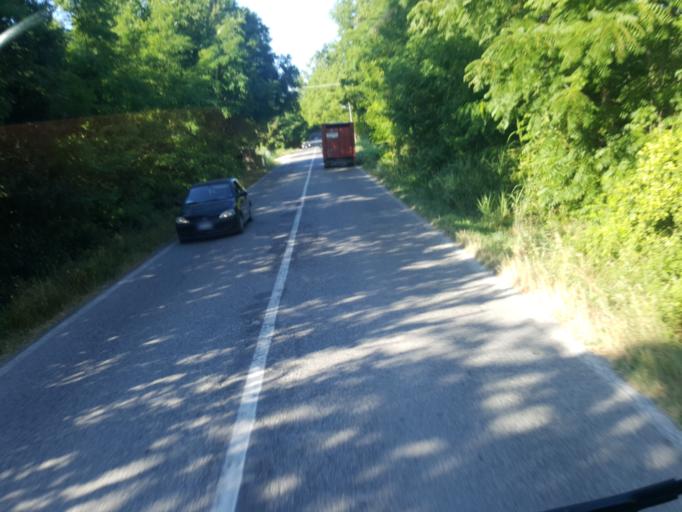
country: IT
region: The Marches
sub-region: Provincia di Pesaro e Urbino
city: Borgo Massano
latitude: 43.8033
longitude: 12.6603
